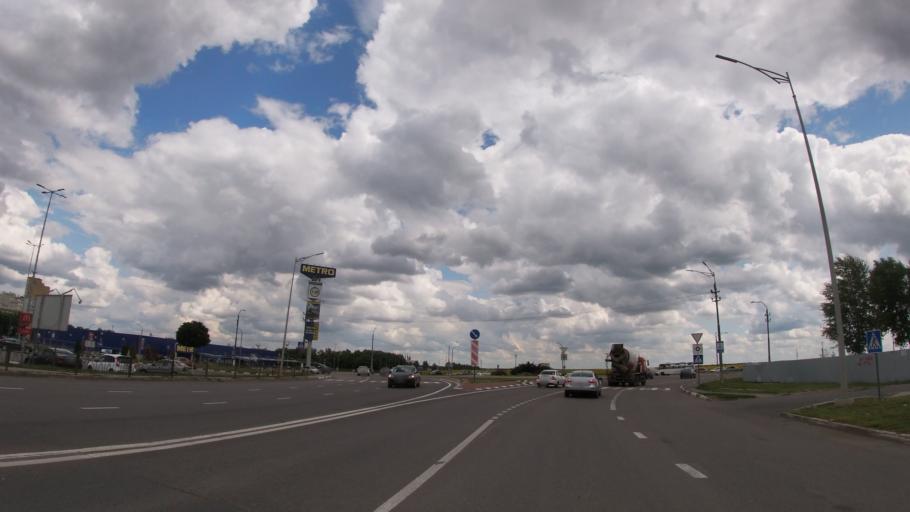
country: RU
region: Belgorod
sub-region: Belgorodskiy Rayon
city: Belgorod
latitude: 50.5512
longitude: 36.5718
